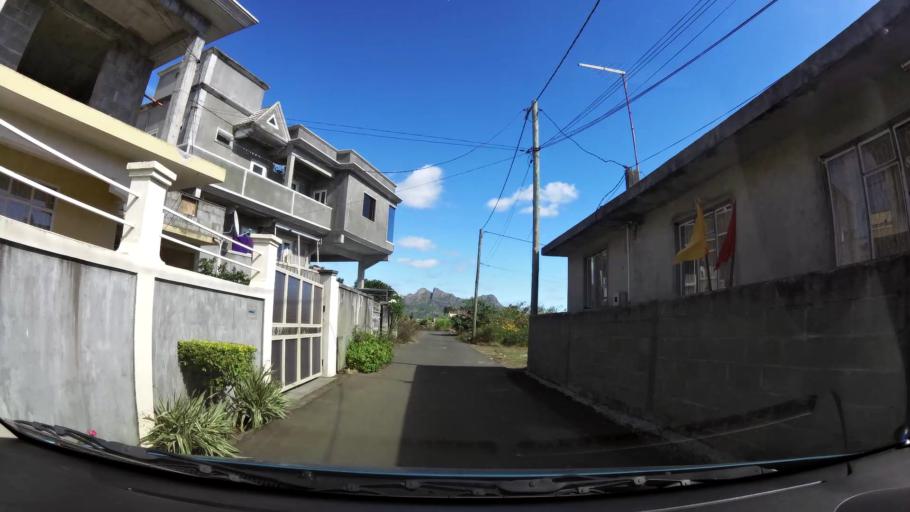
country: MU
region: Plaines Wilhems
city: Vacoas
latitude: -20.2819
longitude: 57.4721
